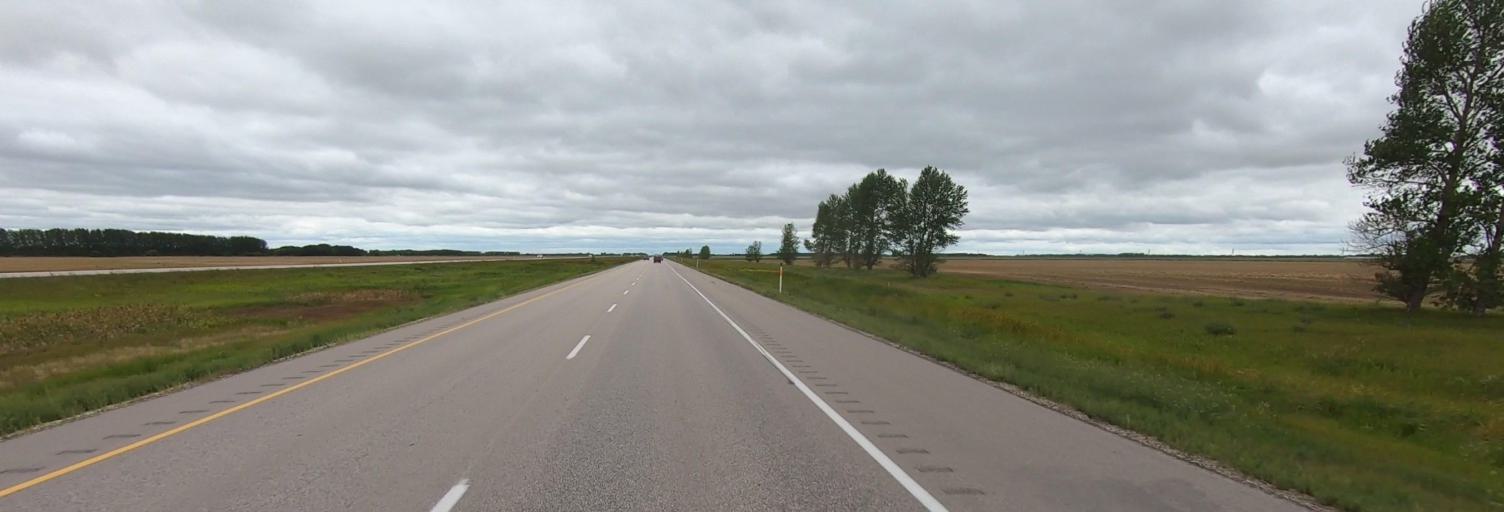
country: CA
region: Manitoba
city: Headingley
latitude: 49.9204
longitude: -97.8291
